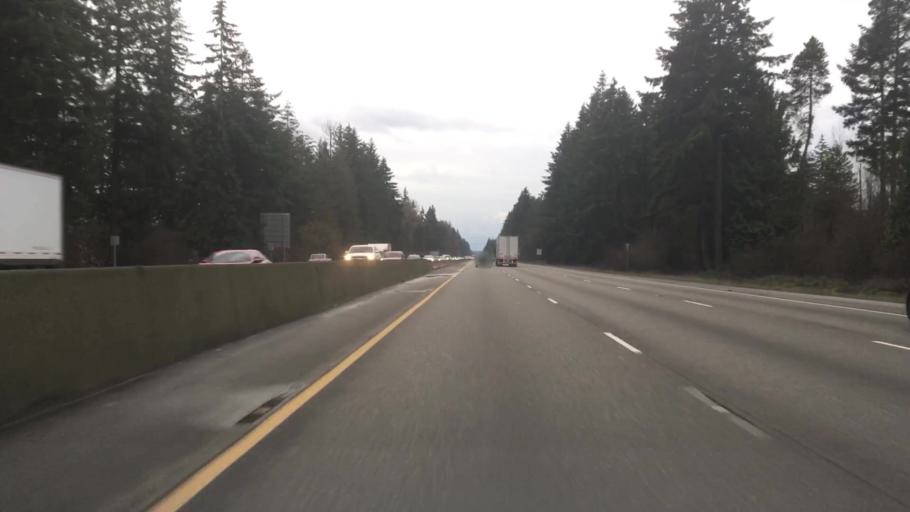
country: US
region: Washington
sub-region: Thurston County
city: Tumwater
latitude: 46.9735
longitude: -122.9315
